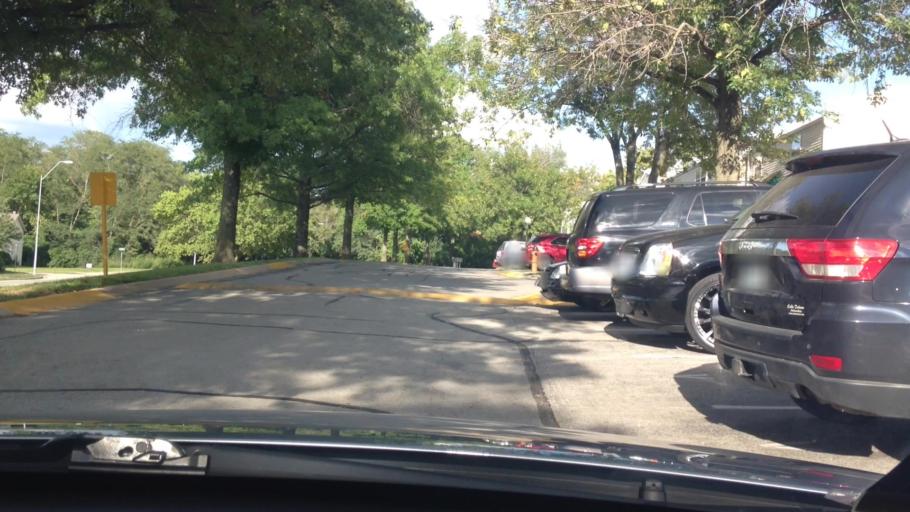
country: US
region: Missouri
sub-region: Clay County
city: Claycomo
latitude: 39.1689
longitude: -94.5096
